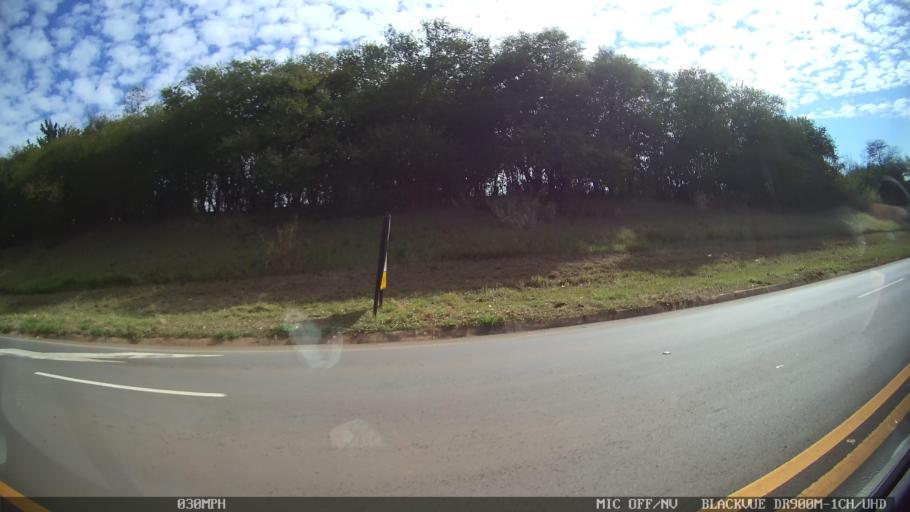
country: BR
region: Sao Paulo
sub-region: Santa Barbara D'Oeste
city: Santa Barbara d'Oeste
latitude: -22.7429
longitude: -47.4257
